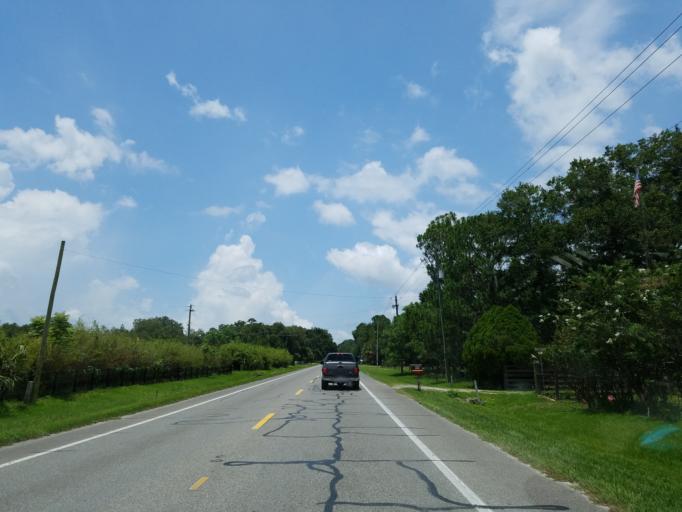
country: US
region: Florida
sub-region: Hillsborough County
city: Fish Hawk
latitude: 27.8506
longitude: -82.1334
